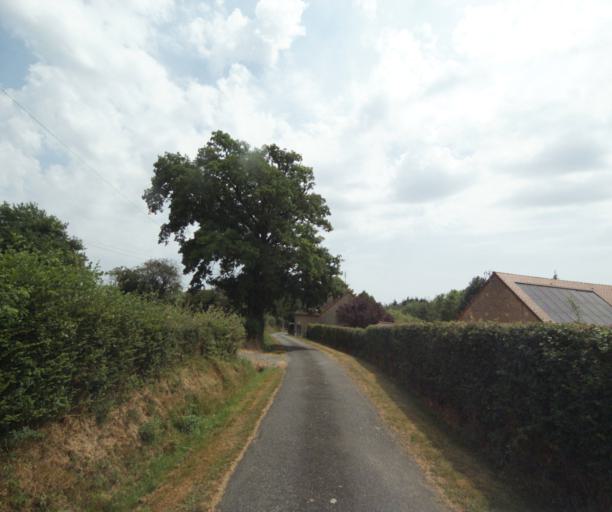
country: FR
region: Bourgogne
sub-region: Departement de Saone-et-Loire
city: Gueugnon
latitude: 46.5823
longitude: 4.0291
